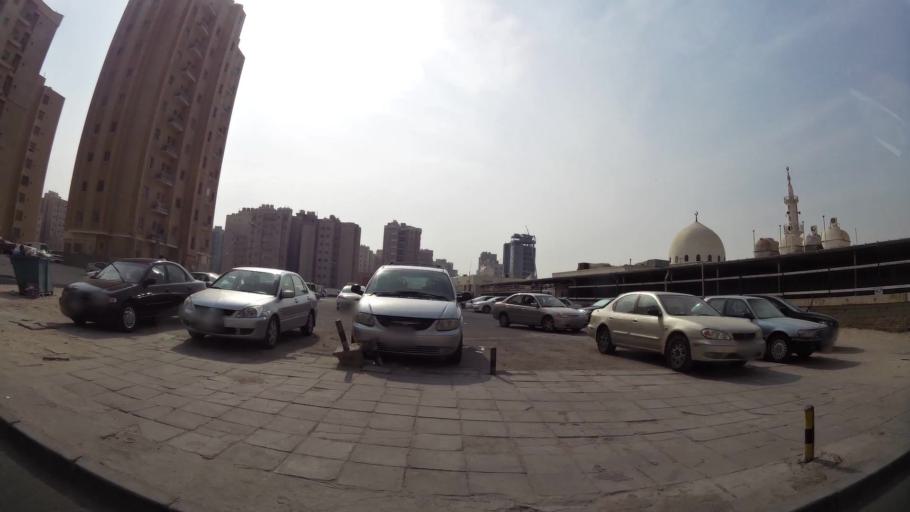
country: KW
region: Al Farwaniyah
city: Al Farwaniyah
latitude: 29.2794
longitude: 47.9580
